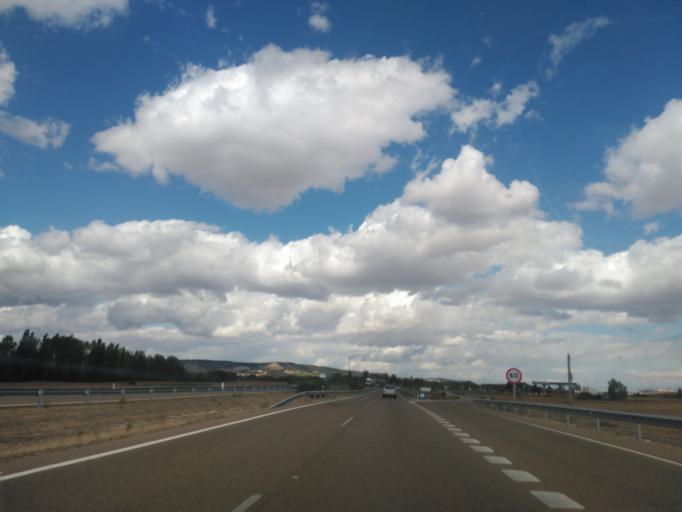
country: ES
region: Castille and Leon
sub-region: Provincia de Palencia
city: Cordovilla la Real
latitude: 42.0451
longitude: -4.2587
